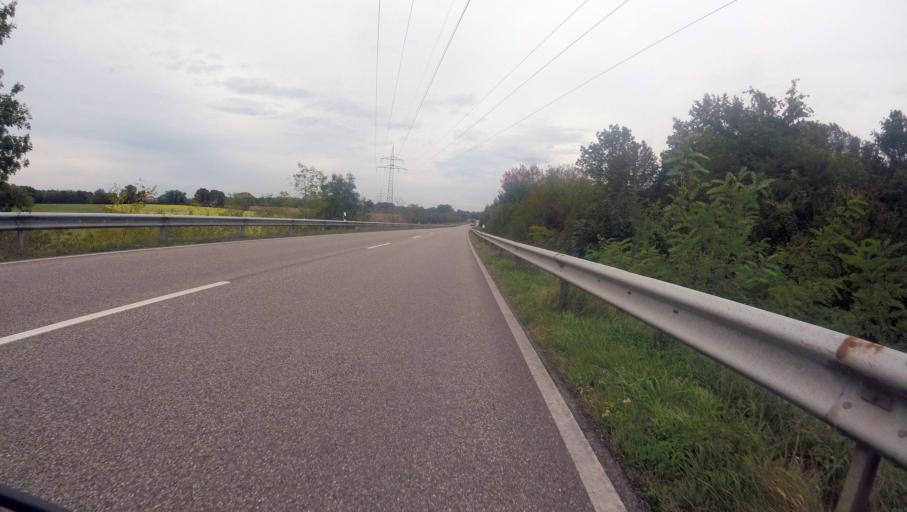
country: DE
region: Baden-Wuerttemberg
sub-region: Karlsruhe Region
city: Iffezheim
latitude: 48.8361
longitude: 8.1668
